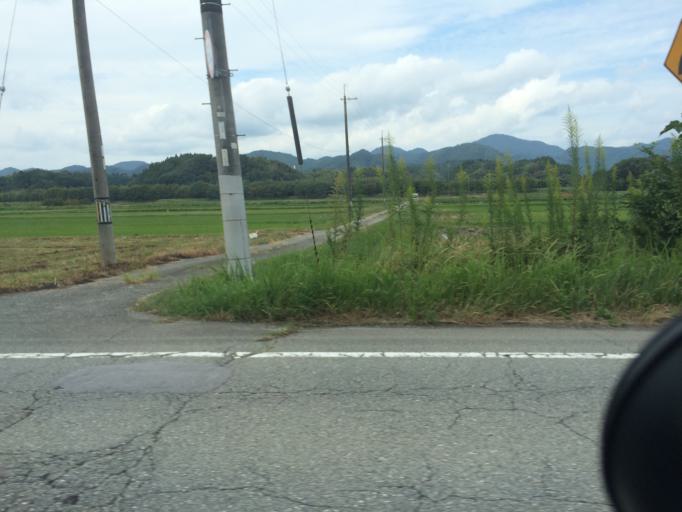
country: JP
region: Hyogo
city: Sasayama
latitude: 35.0686
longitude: 135.2553
